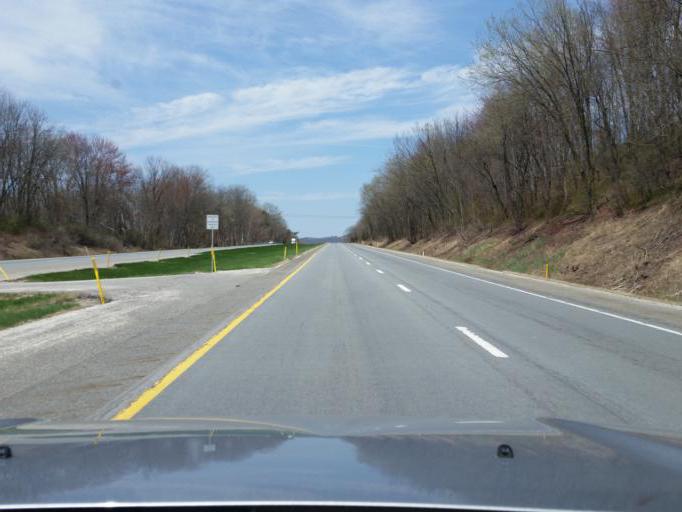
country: US
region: Pennsylvania
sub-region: Perry County
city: Newport
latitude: 40.5184
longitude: -77.1291
